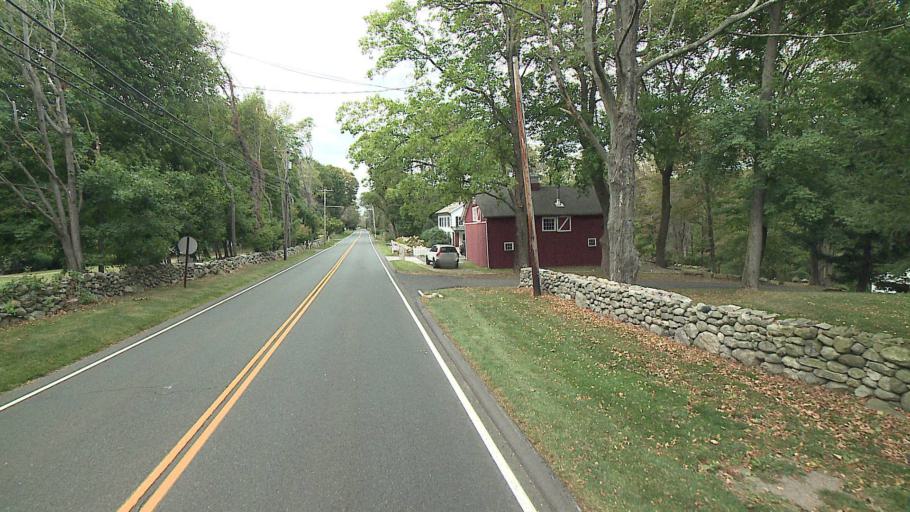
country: US
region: Connecticut
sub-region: Fairfield County
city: Wilton
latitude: 41.2257
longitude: -73.4777
